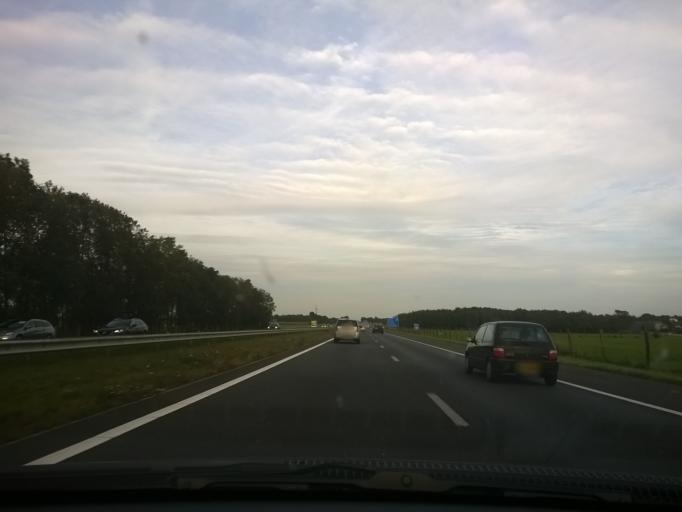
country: NL
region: Groningen
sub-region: Gemeente Grootegast
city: Grootegast
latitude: 53.1473
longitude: 6.2480
